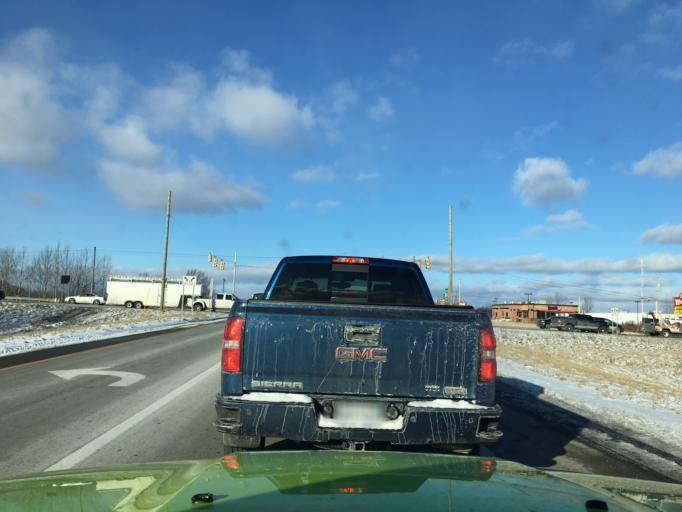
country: US
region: Michigan
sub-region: Kent County
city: Cedar Springs
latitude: 43.2192
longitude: -85.5724
